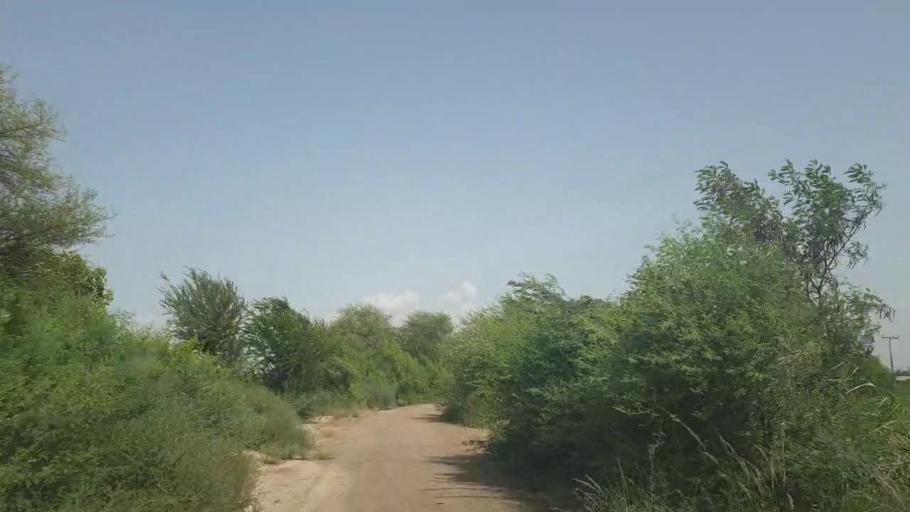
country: PK
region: Sindh
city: Tando Bago
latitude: 24.7516
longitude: 69.1826
